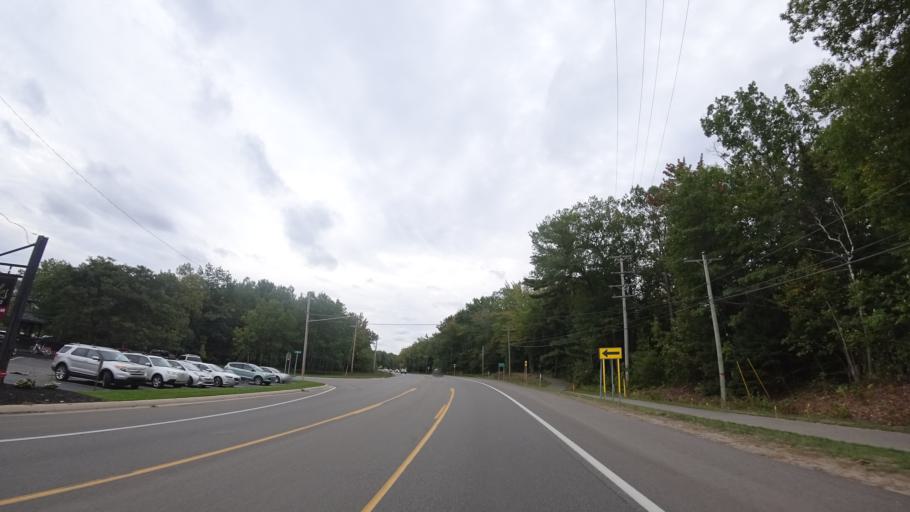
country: US
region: Michigan
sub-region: Emmet County
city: Petoskey
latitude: 45.4138
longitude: -84.9045
